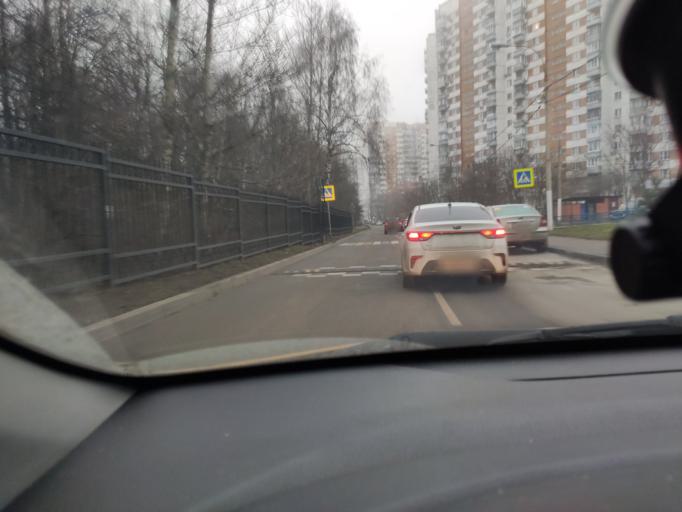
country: RU
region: Moscow
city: Chertanovo Yuzhnoye
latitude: 55.5921
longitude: 37.5919
